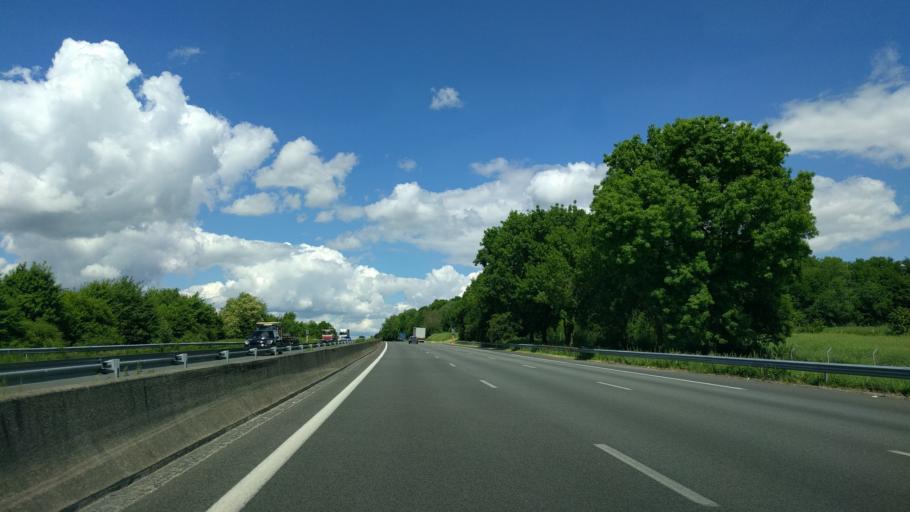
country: FR
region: Picardie
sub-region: Departement de l'Oise
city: Ressons-sur-Matz
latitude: 49.6063
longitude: 2.7549
